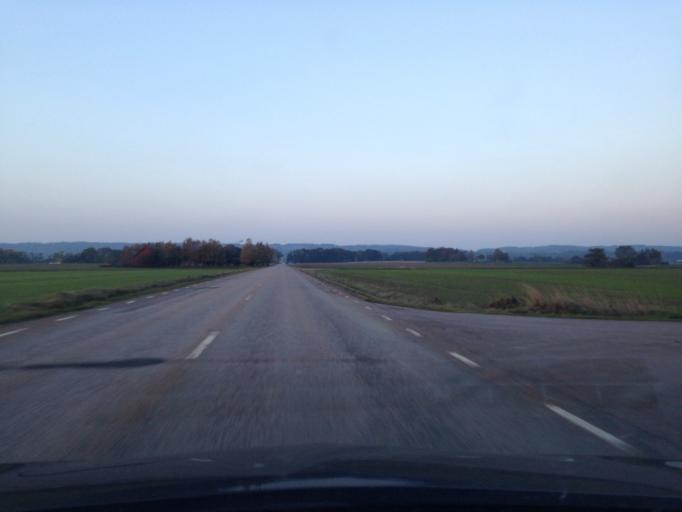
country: SE
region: Skane
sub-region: Angelholms Kommun
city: AEngelholm
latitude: 56.3101
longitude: 12.8851
